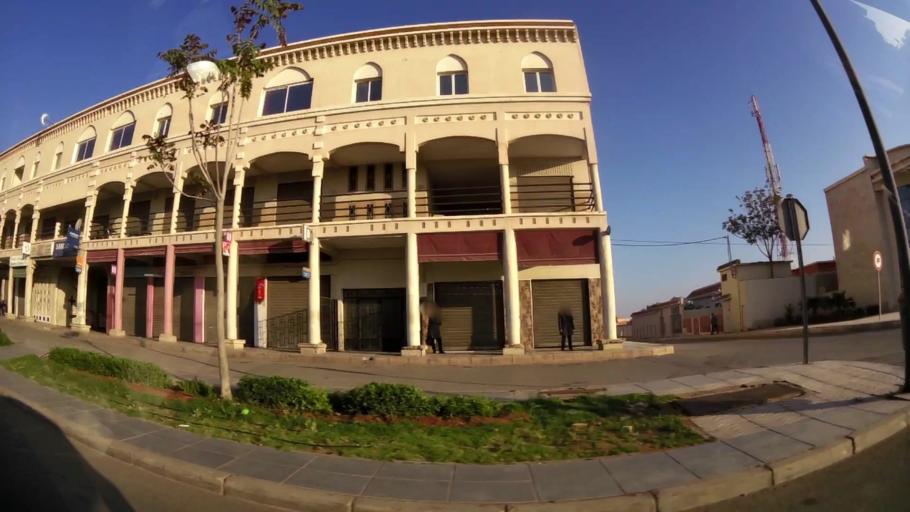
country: MA
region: Oriental
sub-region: Oujda-Angad
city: Oujda
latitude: 34.6743
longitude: -1.9316
